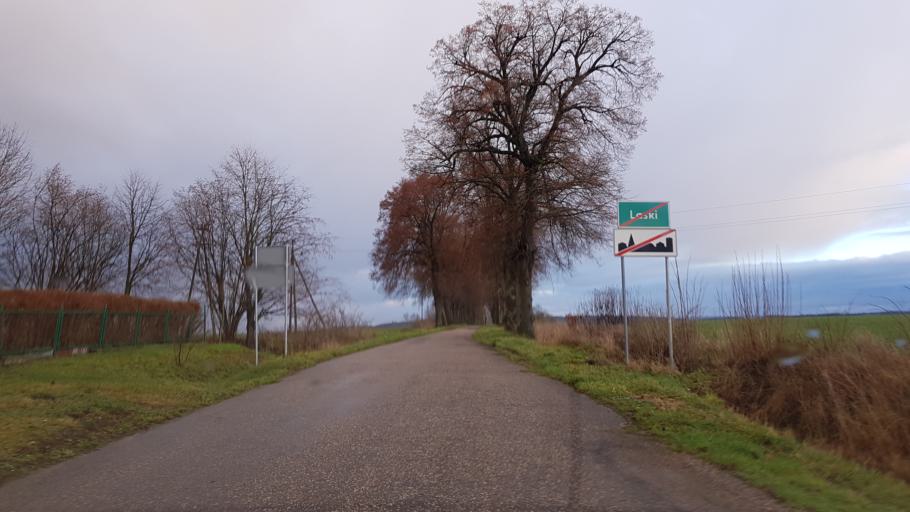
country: PL
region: West Pomeranian Voivodeship
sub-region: Powiat swidwinski
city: Rabino
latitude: 53.9444
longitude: 15.9221
